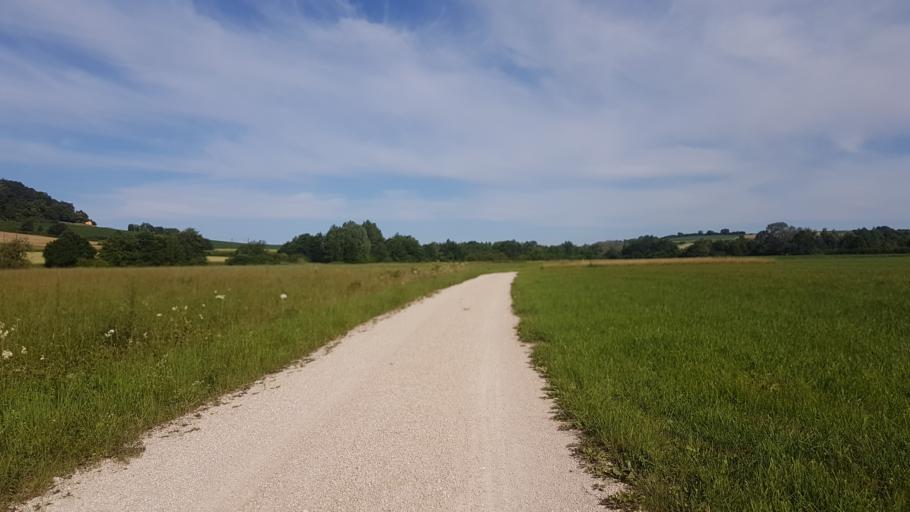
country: DE
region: Bavaria
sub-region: Regierungsbezirk Mittelfranken
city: Treuchtlingen
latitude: 48.9746
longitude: 10.9143
